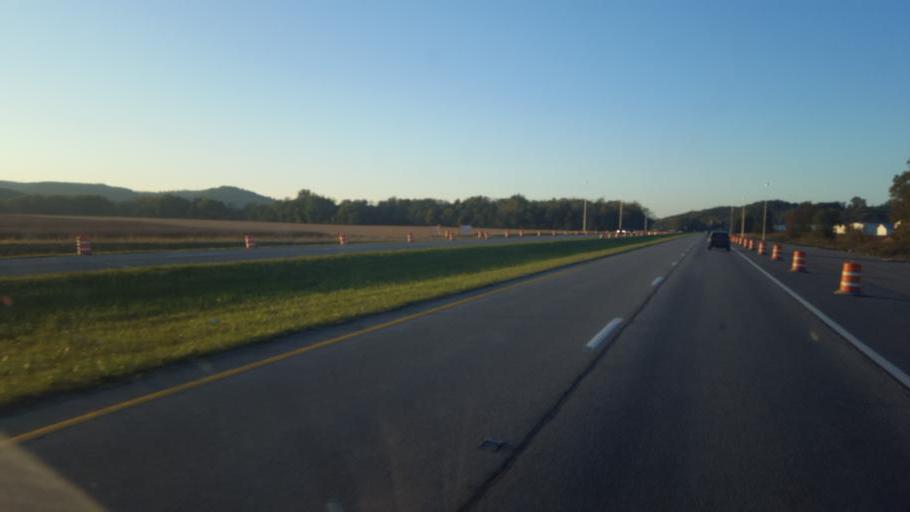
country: US
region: Ohio
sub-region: Scioto County
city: Lucasville
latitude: 38.8960
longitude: -83.0018
